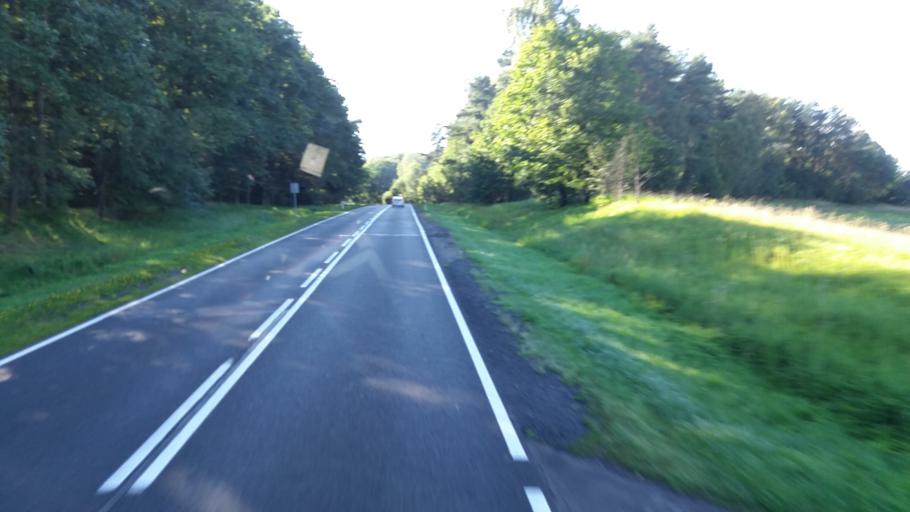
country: PL
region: West Pomeranian Voivodeship
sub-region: Powiat drawski
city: Kalisz Pomorski
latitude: 53.2945
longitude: 15.8545
